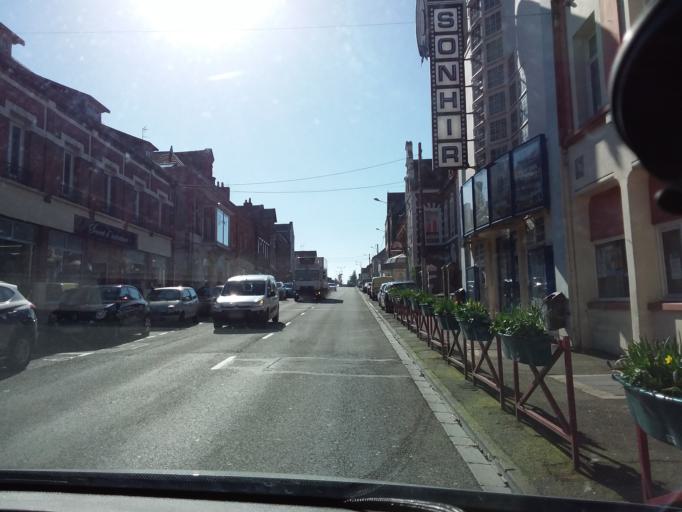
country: FR
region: Picardie
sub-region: Departement de l'Aisne
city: Hirson
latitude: 49.9202
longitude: 4.0842
